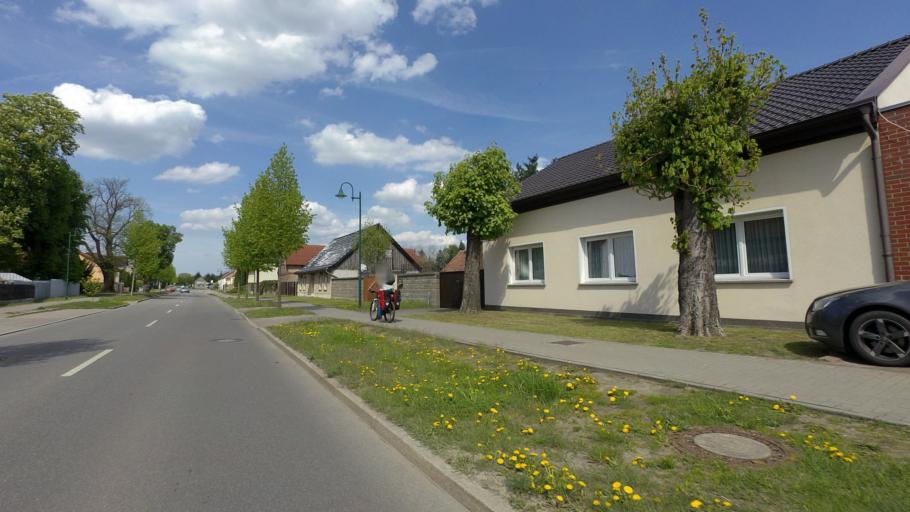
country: DE
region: Brandenburg
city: Wandlitz
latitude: 52.7949
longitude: 13.4797
